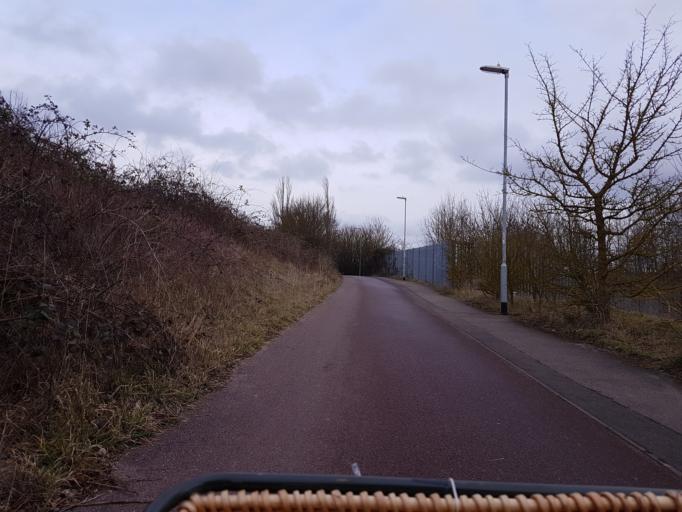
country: GB
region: England
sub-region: Cambridgeshire
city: Cambridge
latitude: 52.1939
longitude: 0.1680
